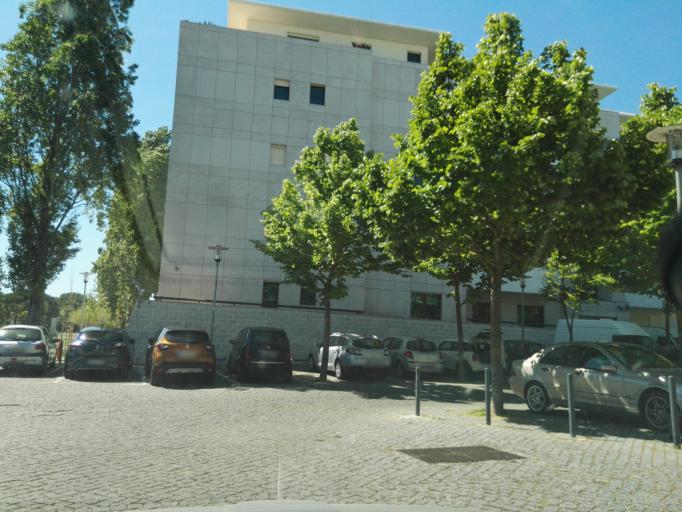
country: PT
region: Lisbon
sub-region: Loures
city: Moscavide
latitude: 38.7819
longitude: -9.0935
